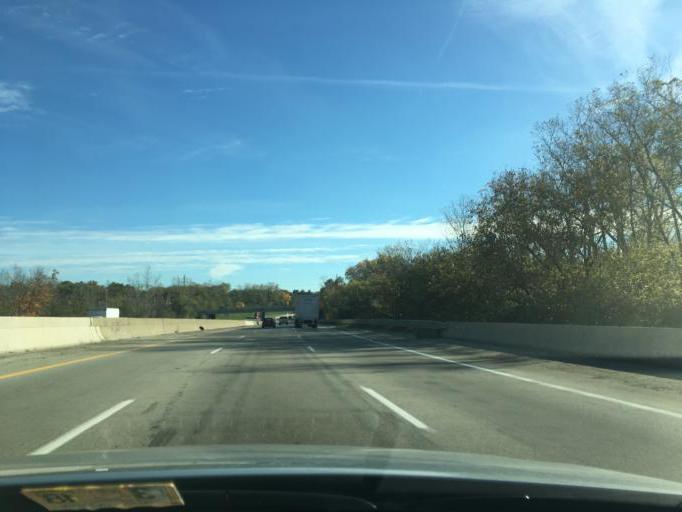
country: US
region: Michigan
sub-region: Wayne County
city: Plymouth
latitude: 42.3901
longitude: -83.4692
